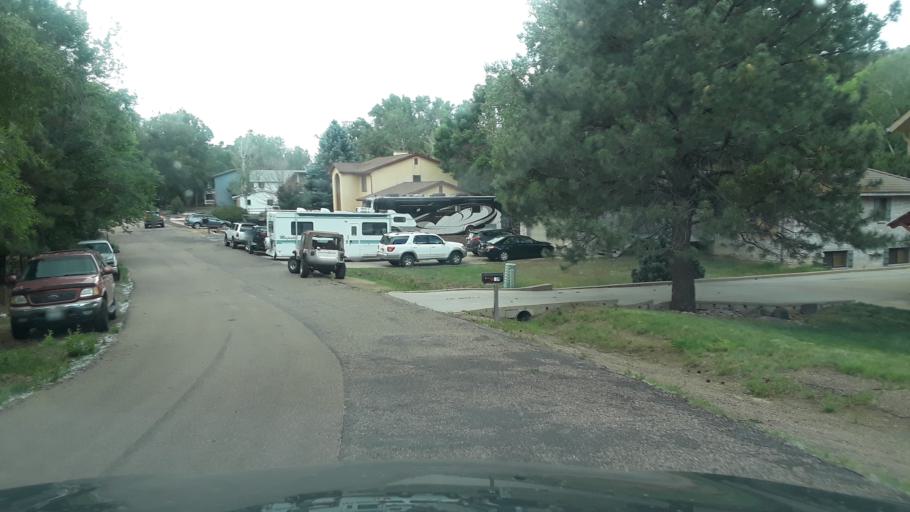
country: US
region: Colorado
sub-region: El Paso County
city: Air Force Academy
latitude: 38.9492
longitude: -104.8271
